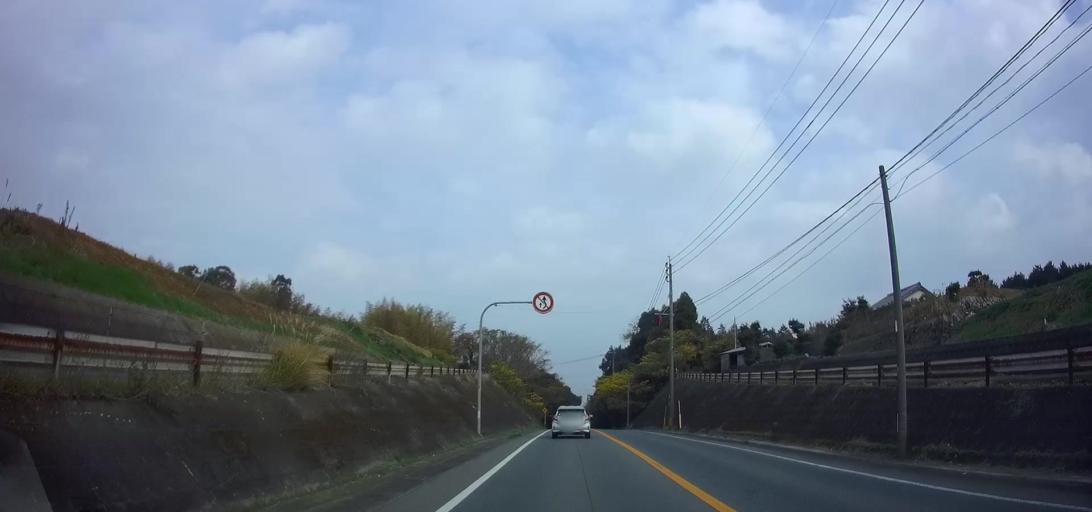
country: JP
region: Nagasaki
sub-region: Isahaya-shi
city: Isahaya
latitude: 32.7870
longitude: 130.0460
